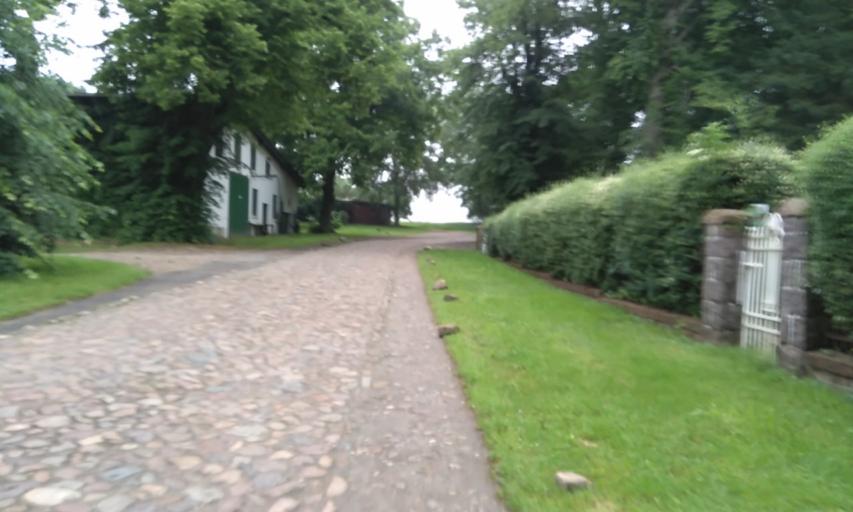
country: DE
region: Lower Saxony
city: Deinste
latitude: 53.5483
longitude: 9.4378
